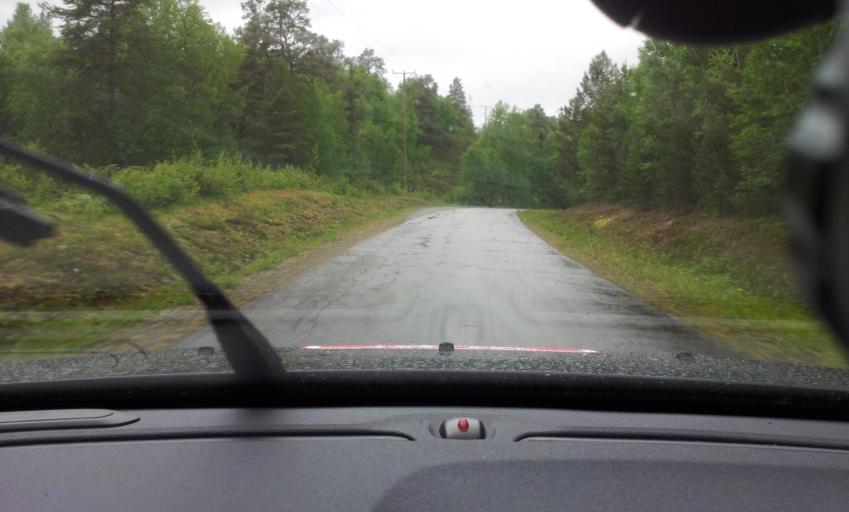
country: SE
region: Jaemtland
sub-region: Are Kommun
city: Are
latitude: 63.1491
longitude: 12.9326
